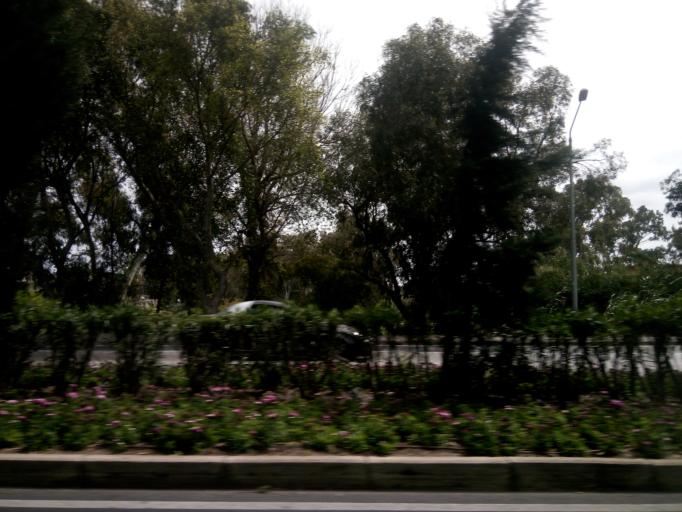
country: MT
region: Il-Marsa
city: Marsa
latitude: 35.8783
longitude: 14.4931
